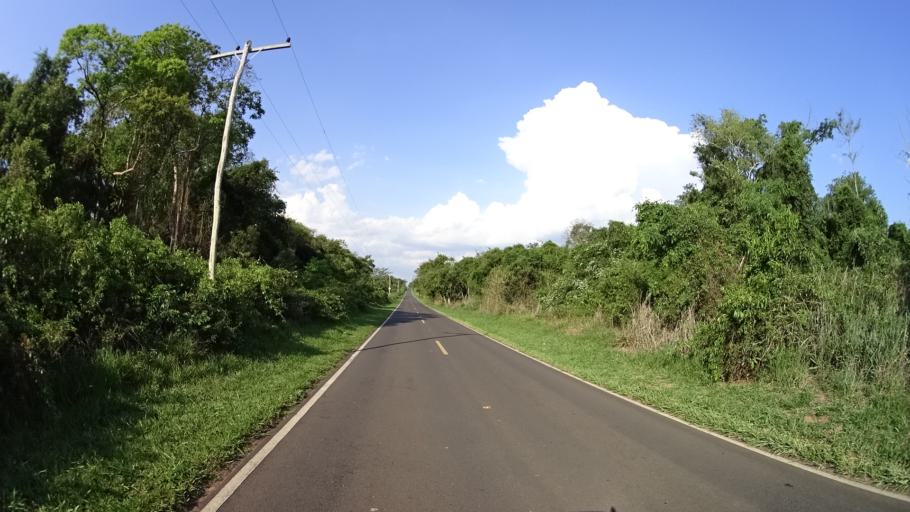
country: BR
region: Sao Paulo
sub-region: Urupes
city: Urupes
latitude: -21.3805
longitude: -49.4873
